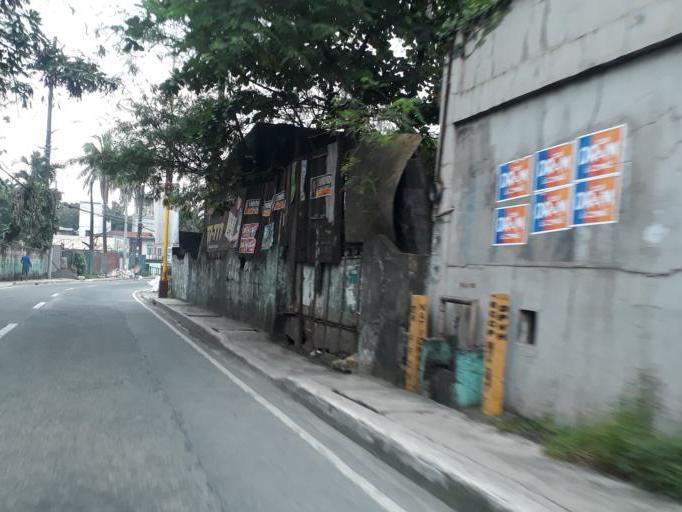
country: PH
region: Calabarzon
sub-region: Province of Rizal
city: Navotas
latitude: 14.6639
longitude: 120.9449
